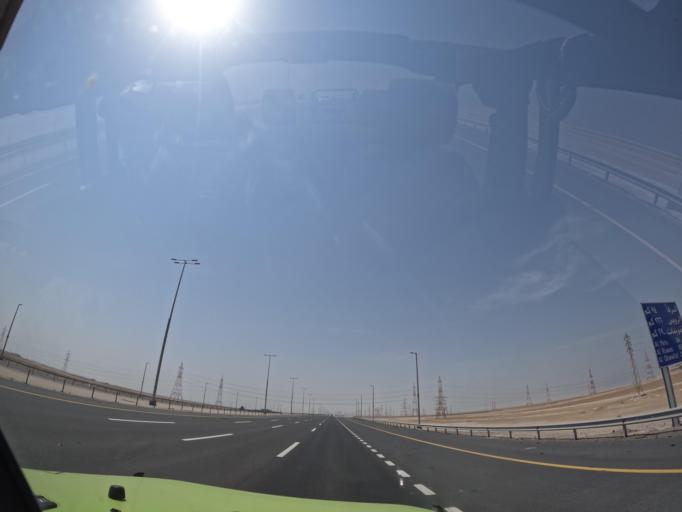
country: AE
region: Abu Dhabi
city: Abu Dhabi
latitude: 24.1562
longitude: 54.3086
